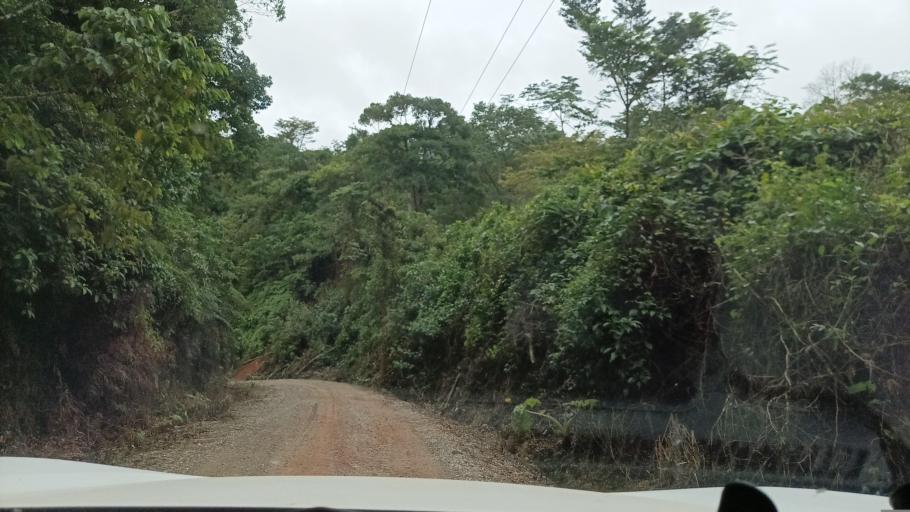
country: MX
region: Veracruz
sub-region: Uxpanapa
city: Poblado 10
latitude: 17.4191
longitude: -94.4174
